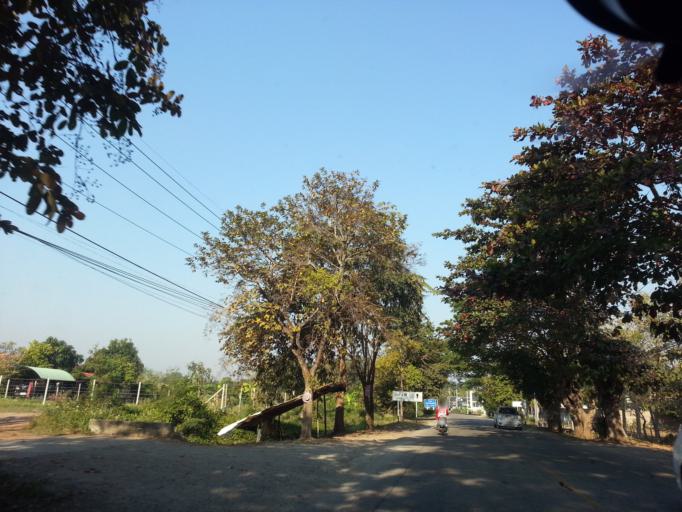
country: TH
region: Chiang Mai
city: San Sai
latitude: 18.8765
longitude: 99.0437
